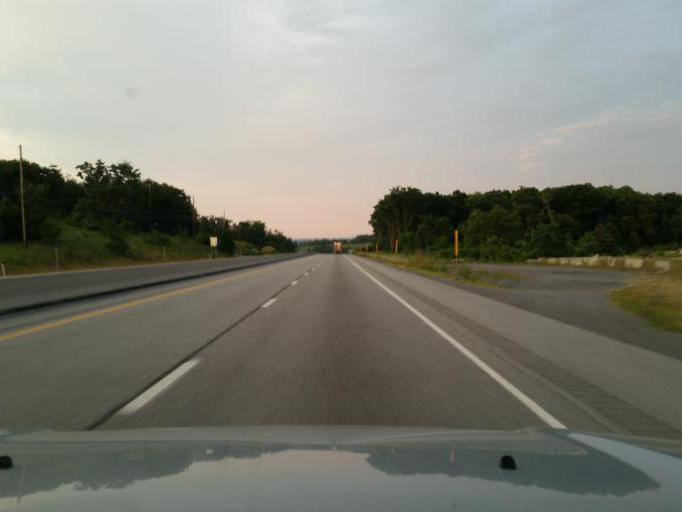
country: US
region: Pennsylvania
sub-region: Cambria County
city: Vinco
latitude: 40.4385
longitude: -78.9001
